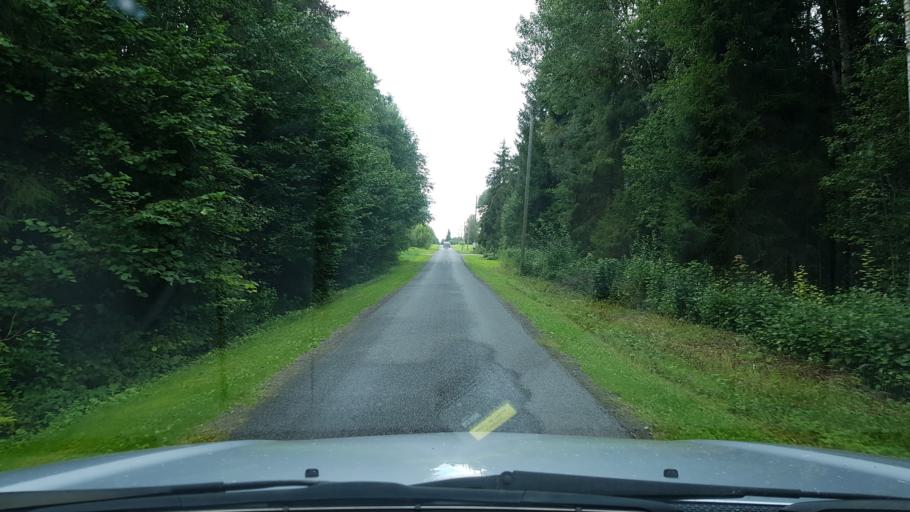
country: EE
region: Harju
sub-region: Raasiku vald
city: Arukula
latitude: 59.3010
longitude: 25.0464
